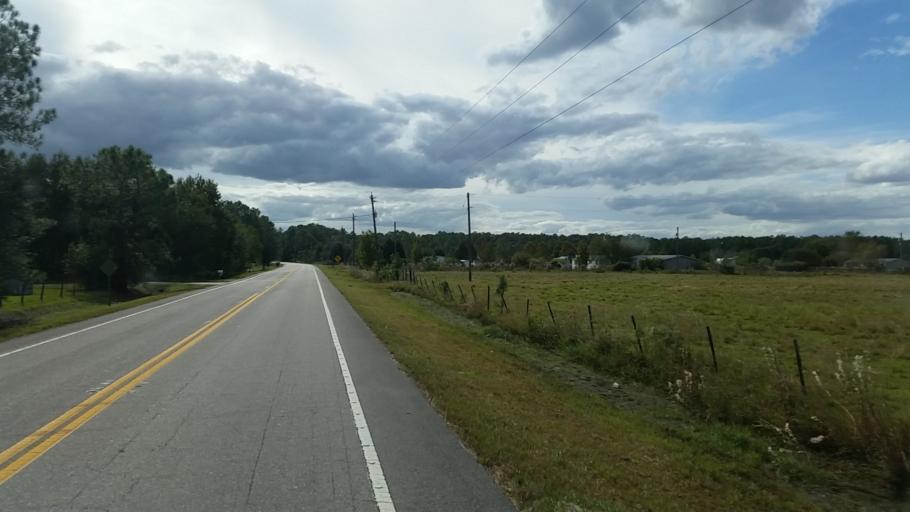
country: US
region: Florida
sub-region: Polk County
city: Gibsonia
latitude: 28.2549
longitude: -81.9623
